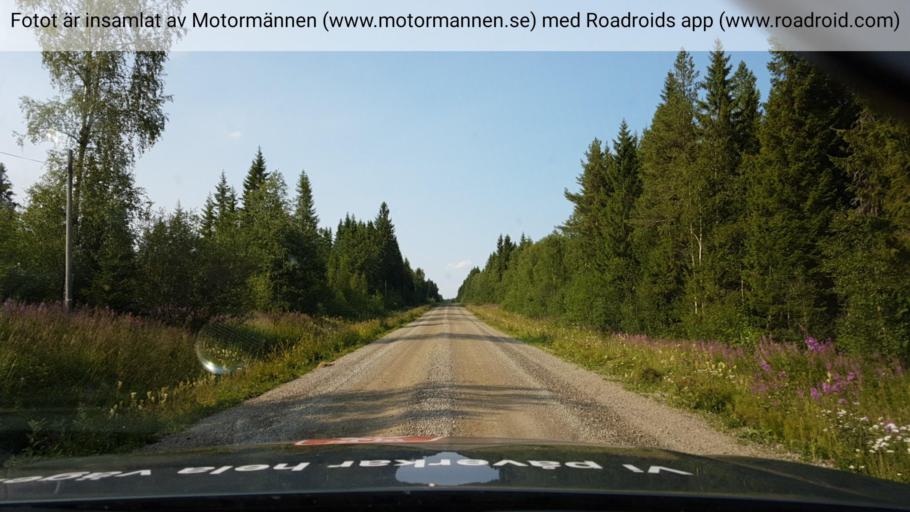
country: SE
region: Jaemtland
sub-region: OEstersunds Kommun
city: Brunflo
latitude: 62.6203
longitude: 14.9448
